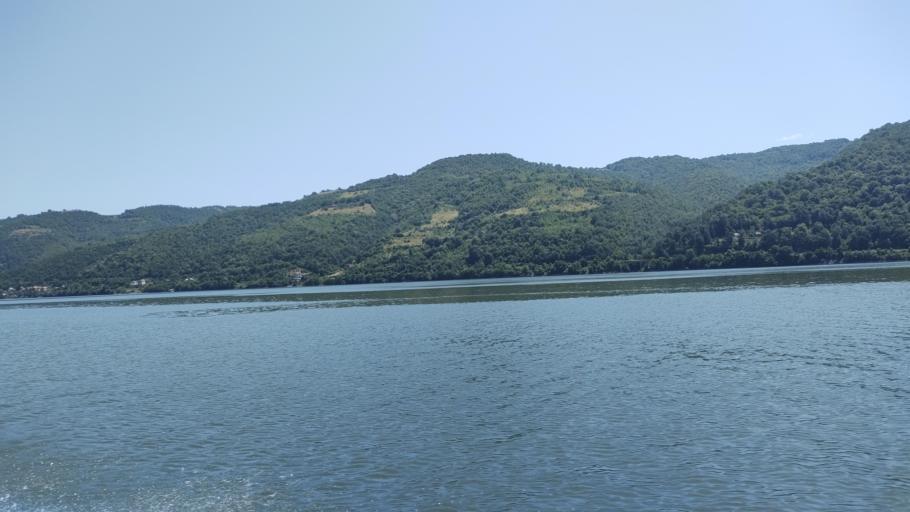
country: RO
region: Mehedinti
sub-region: Comuna Svinita
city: Svinita
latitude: 44.5182
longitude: 22.2005
